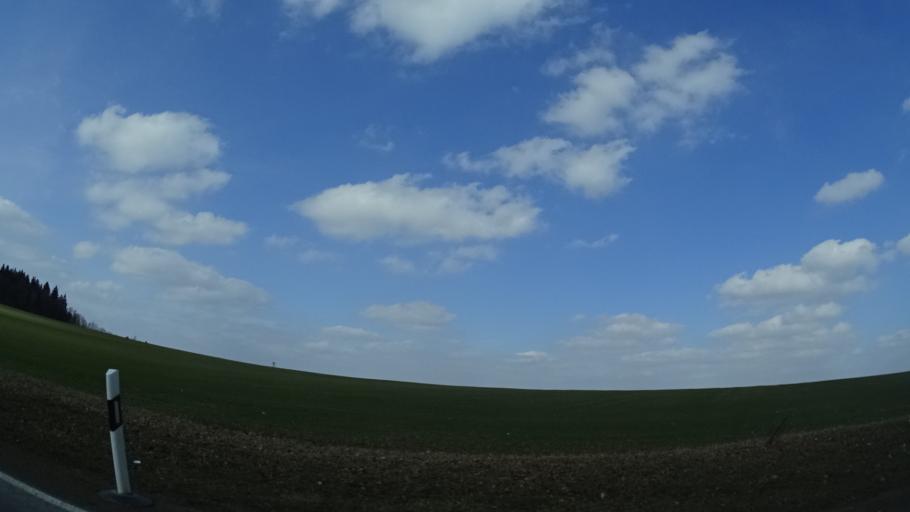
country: DE
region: Thuringia
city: Schleiz
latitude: 50.5504
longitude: 11.8210
